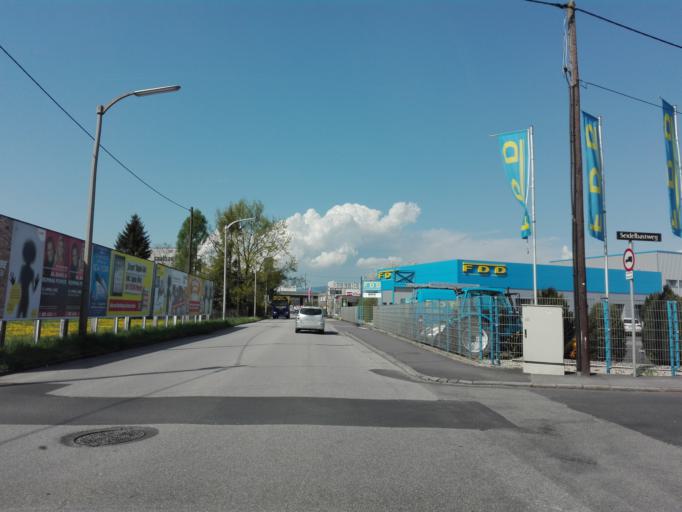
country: AT
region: Upper Austria
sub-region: Politischer Bezirk Linz-Land
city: Leonding
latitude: 48.2498
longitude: 14.2768
